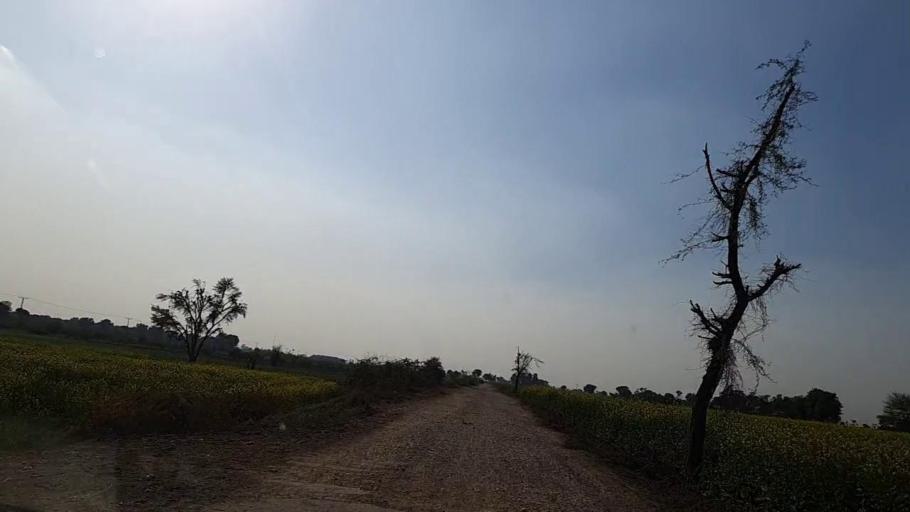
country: PK
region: Sindh
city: Sakrand
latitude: 26.1278
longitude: 68.2610
